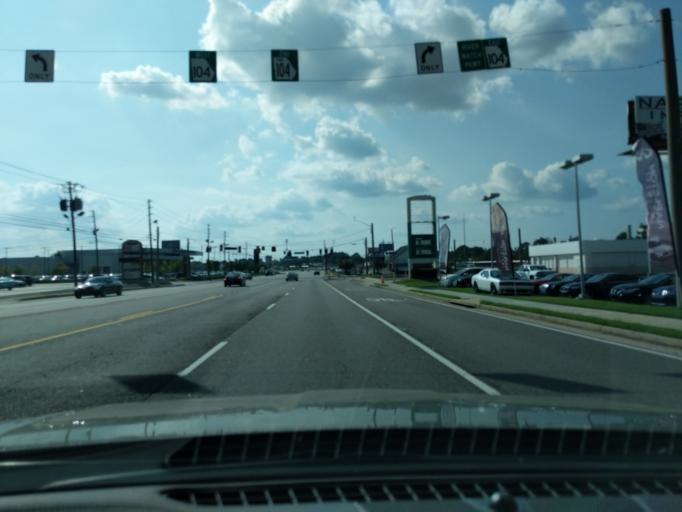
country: US
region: Georgia
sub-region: Columbia County
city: Martinez
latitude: 33.5159
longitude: -82.0691
